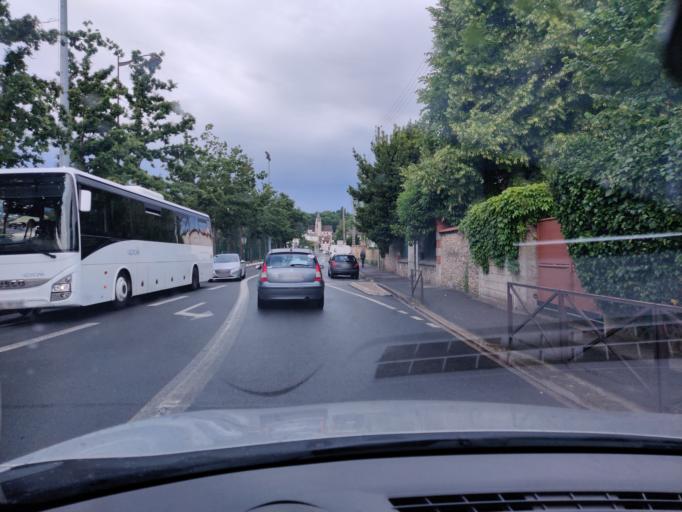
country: FR
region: Ile-de-France
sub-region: Departement de l'Essonne
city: Juvisy-sur-Orge
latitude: 48.6730
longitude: 2.3807
